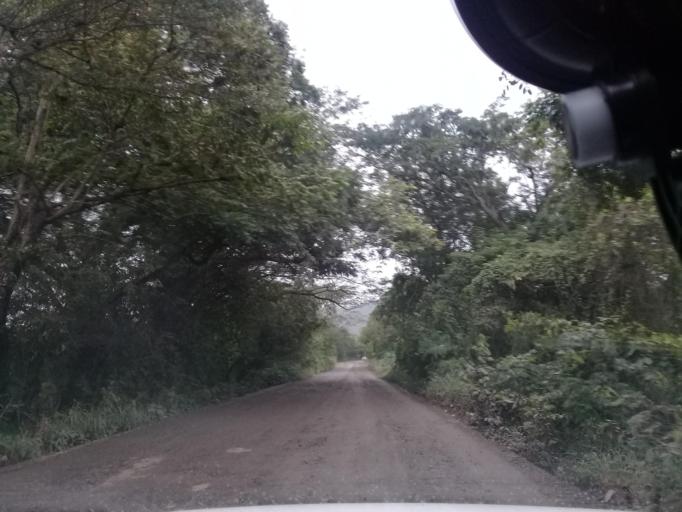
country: MX
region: Veracruz
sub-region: Chalma
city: San Pedro Coyutla
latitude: 21.2223
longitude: -98.3815
